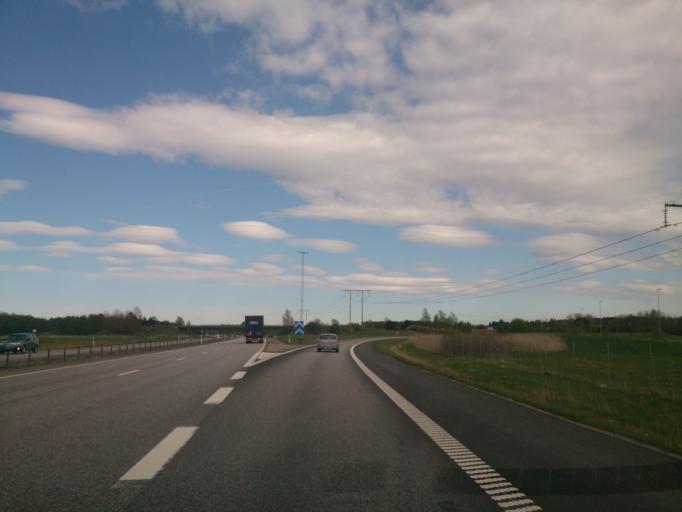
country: SE
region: OEstergoetland
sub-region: Linkopings Kommun
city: Ekangen
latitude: 58.4323
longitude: 15.6630
